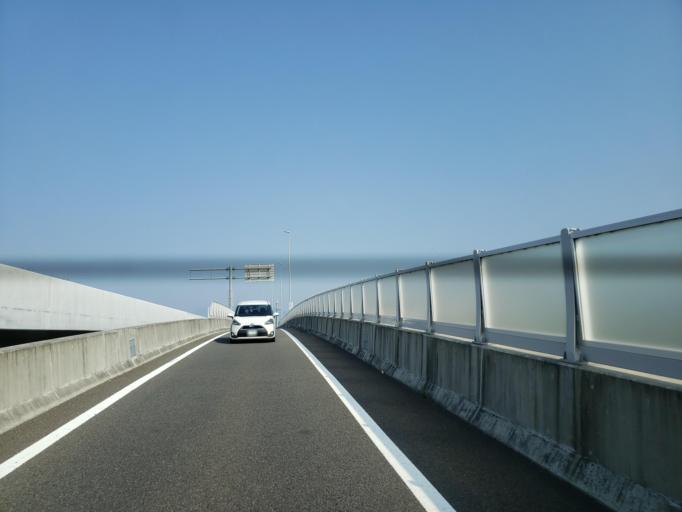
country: JP
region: Ehime
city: Masaki-cho
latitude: 33.8088
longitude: 132.7367
